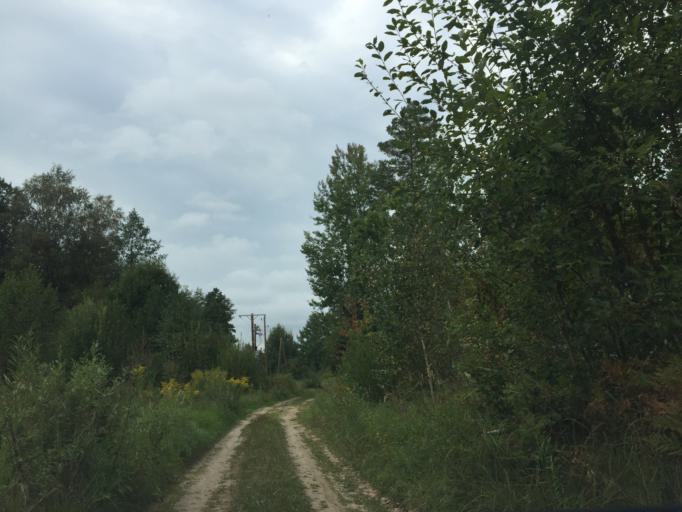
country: LV
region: Baldone
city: Baldone
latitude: 56.7671
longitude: 24.4576
